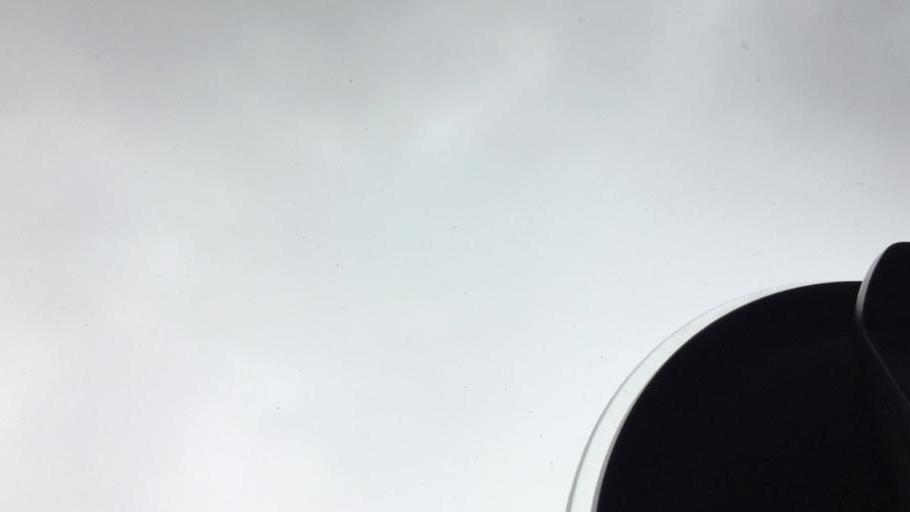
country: US
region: Georgia
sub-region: Clayton County
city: Morrow
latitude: 33.5727
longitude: -84.3316
